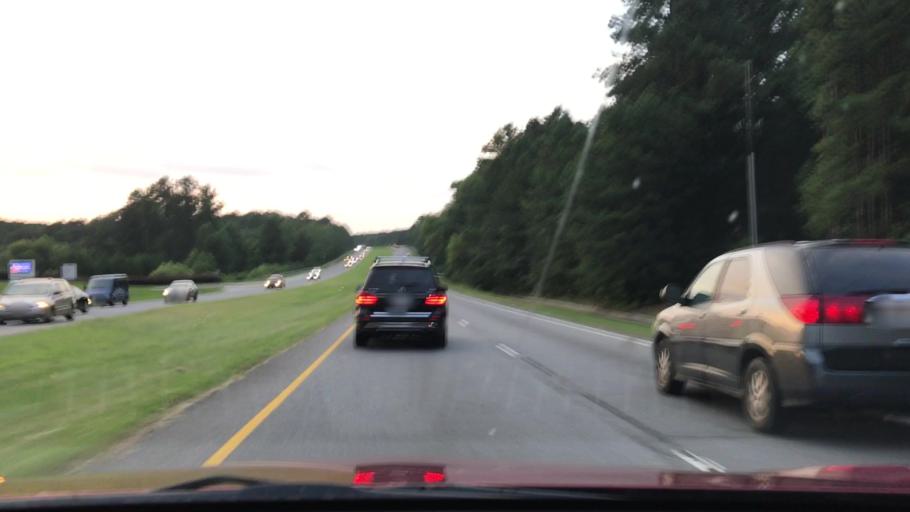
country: US
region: Georgia
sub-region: Gwinnett County
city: Lawrenceville
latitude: 34.0242
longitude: -83.9862
